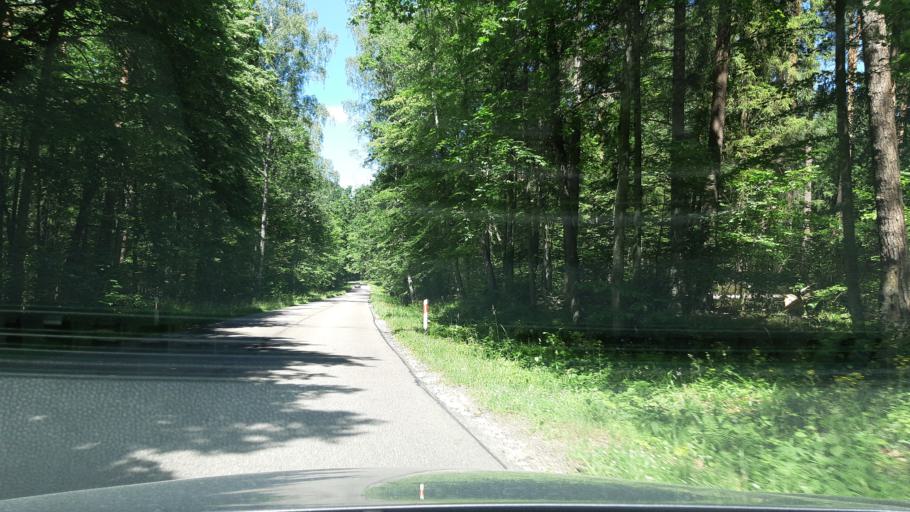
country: PL
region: Warmian-Masurian Voivodeship
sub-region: Powiat mragowski
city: Mikolajki
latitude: 53.7489
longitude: 21.5032
